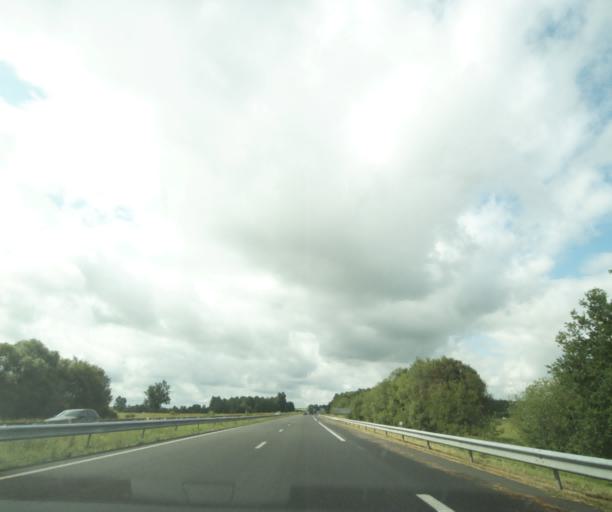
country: FR
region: Pays de la Loire
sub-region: Departement de Maine-et-Loire
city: Durtal
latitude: 47.6901
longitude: -0.2503
